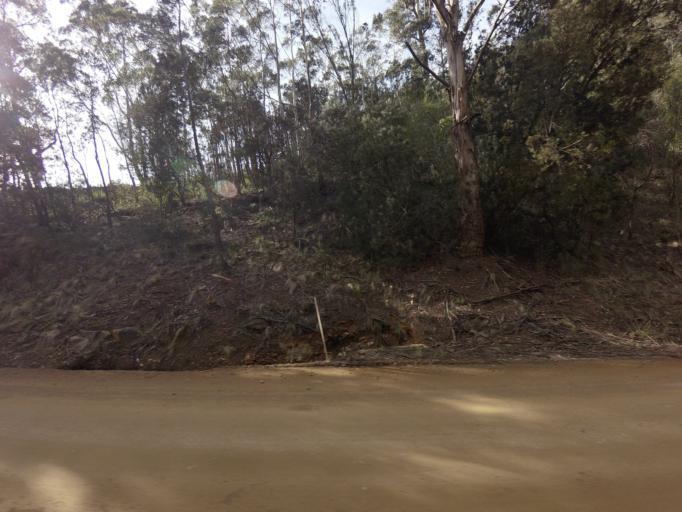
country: AU
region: Tasmania
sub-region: Huon Valley
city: Huonville
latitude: -43.0658
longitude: 147.0904
